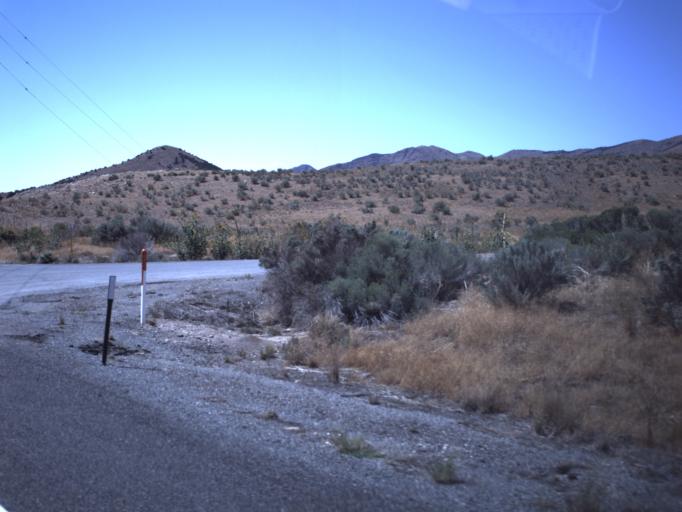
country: US
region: Utah
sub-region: Juab County
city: Nephi
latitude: 39.6097
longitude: -112.1354
